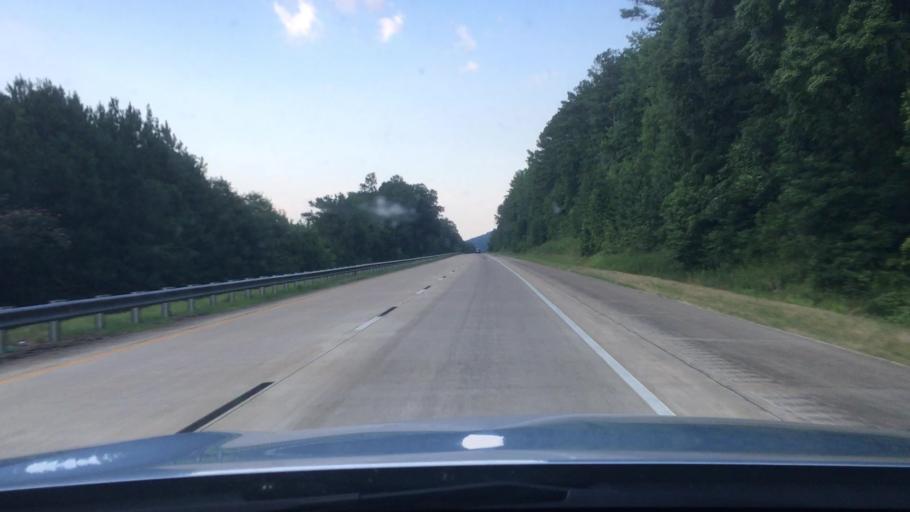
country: US
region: Alabama
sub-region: Etowah County
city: Whitesboro
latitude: 34.1071
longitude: -85.9946
